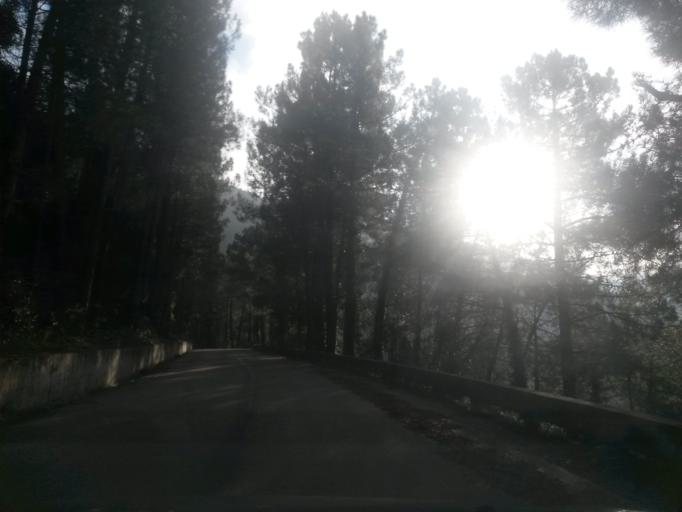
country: ES
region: Catalonia
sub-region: Provincia de Girona
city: Susqueda
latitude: 41.9815
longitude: 2.5298
